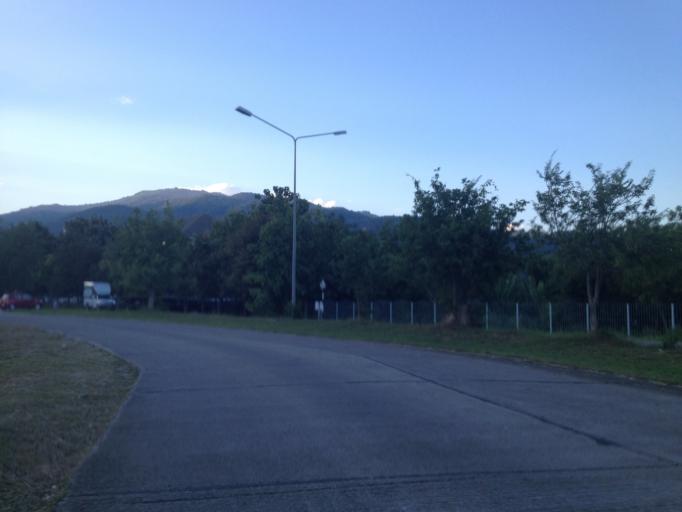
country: TH
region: Chiang Mai
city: Chiang Mai
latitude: 18.7600
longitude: 98.9376
